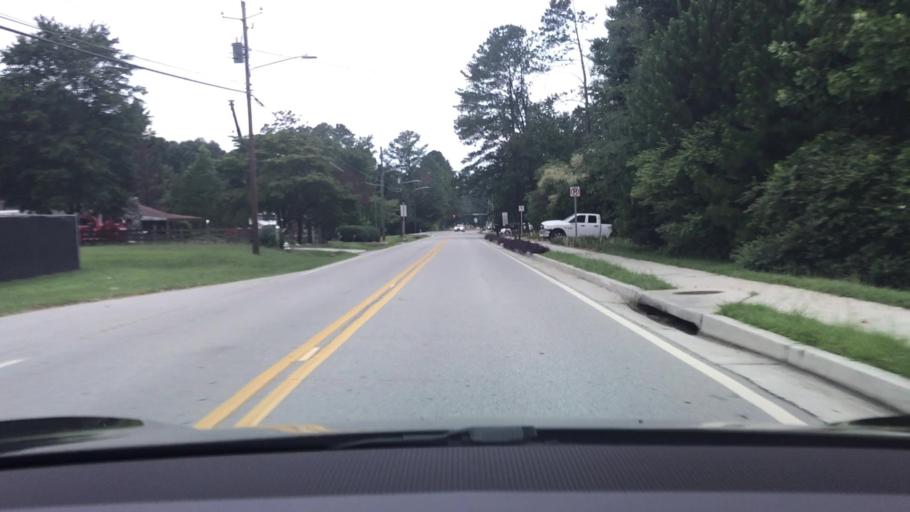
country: US
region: Georgia
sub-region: Gwinnett County
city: Suwanee
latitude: 34.0878
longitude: -84.0703
